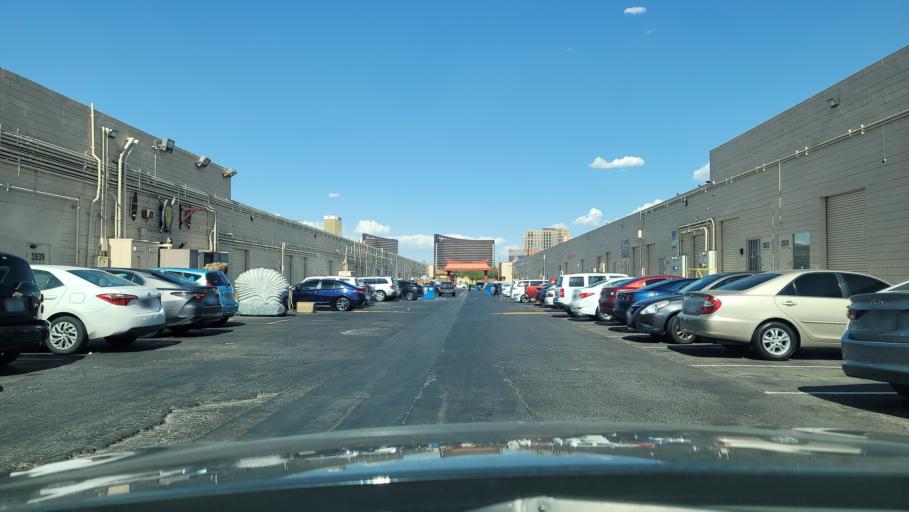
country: US
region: Nevada
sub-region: Clark County
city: Paradise
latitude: 36.1259
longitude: -115.1927
